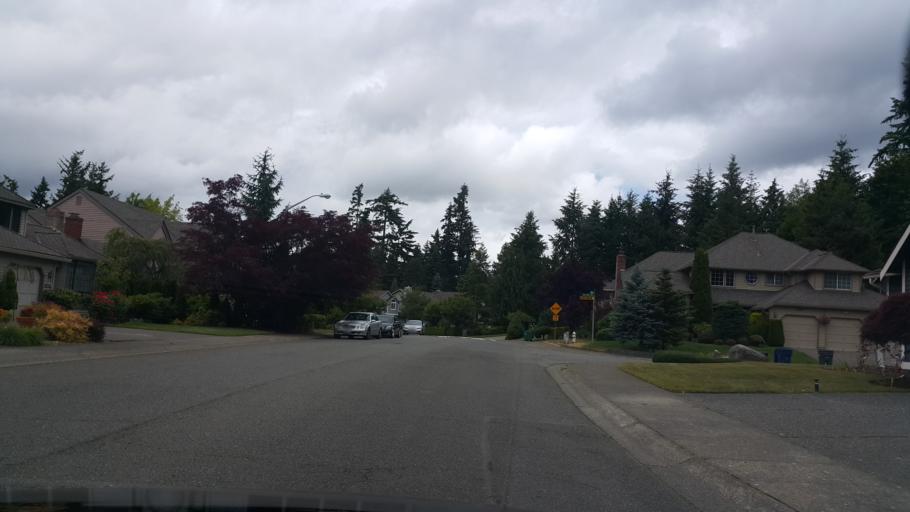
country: US
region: Washington
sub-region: King County
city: Fairwood
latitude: 47.4388
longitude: -122.1521
